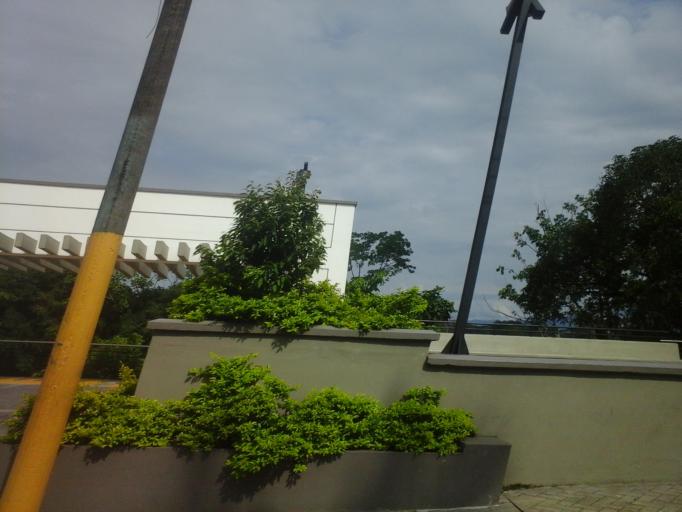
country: CO
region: Putumayo
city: Puerto Guzman
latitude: 0.8606
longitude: -76.5809
